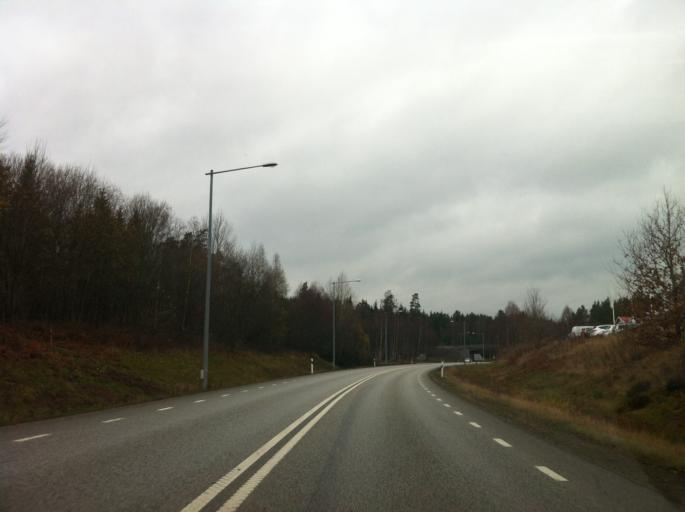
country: SE
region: Joenkoeping
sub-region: Vetlanda Kommun
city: Vetlanda
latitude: 57.4111
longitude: 15.0701
